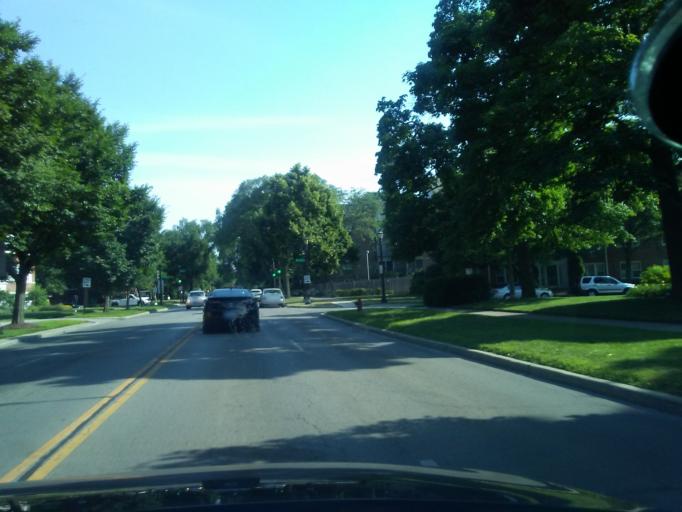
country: US
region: Illinois
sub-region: Cook County
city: Evanston
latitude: 42.0238
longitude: -87.6852
